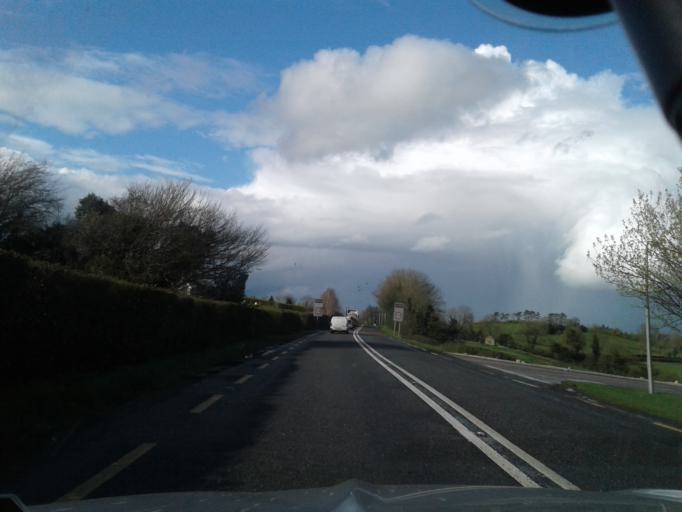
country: IE
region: Ulster
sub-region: County Monaghan
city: Monaghan
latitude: 54.3463
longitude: -6.9624
